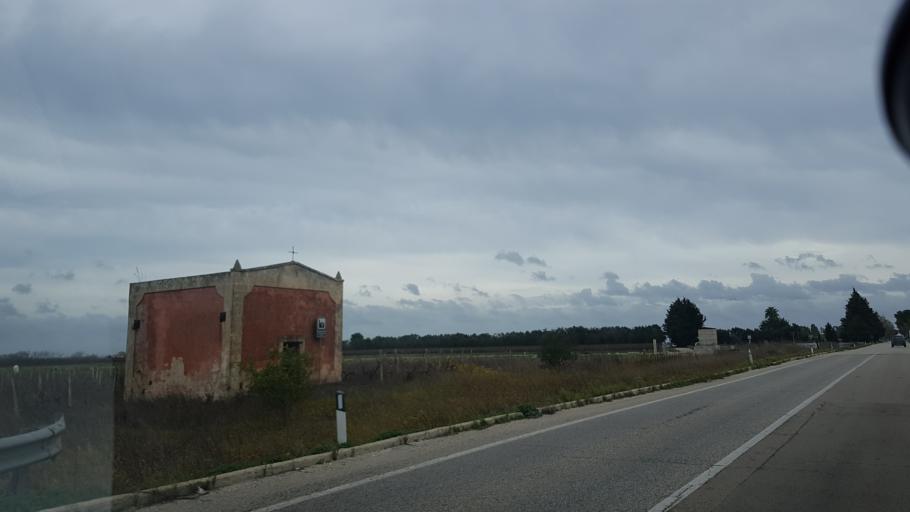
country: IT
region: Apulia
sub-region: Provincia di Brindisi
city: San Pancrazio Salentino
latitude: 40.4139
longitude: 17.8566
